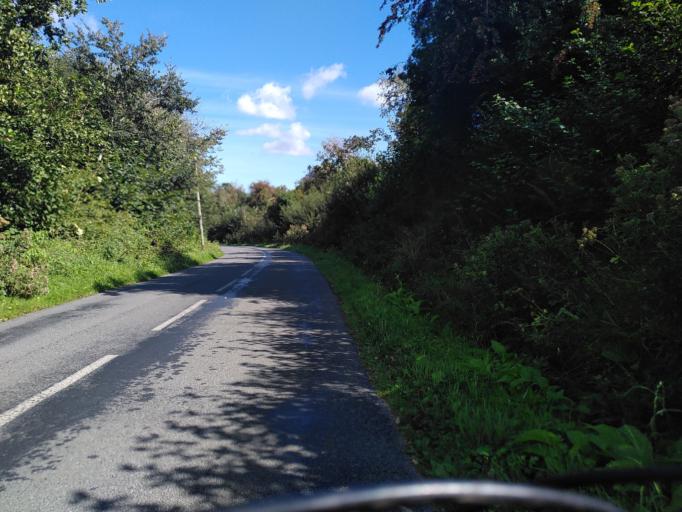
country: FR
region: Nord-Pas-de-Calais
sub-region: Departement du Pas-de-Calais
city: Ambleteuse
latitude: 50.8012
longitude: 1.6288
